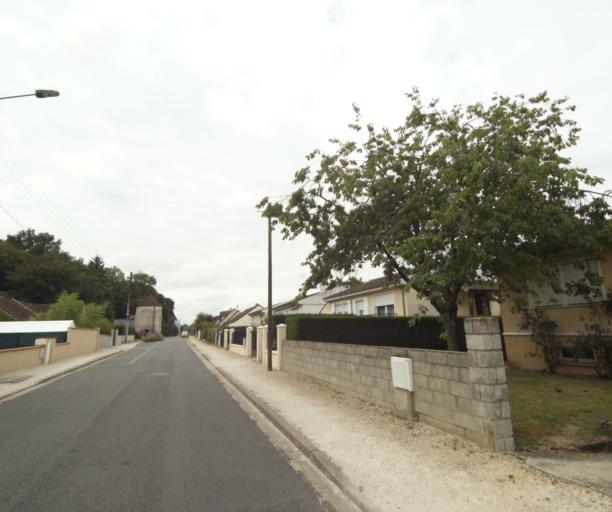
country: FR
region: Centre
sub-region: Departement du Loiret
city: Boigny-sur-Bionne
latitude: 47.9264
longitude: 2.0098
